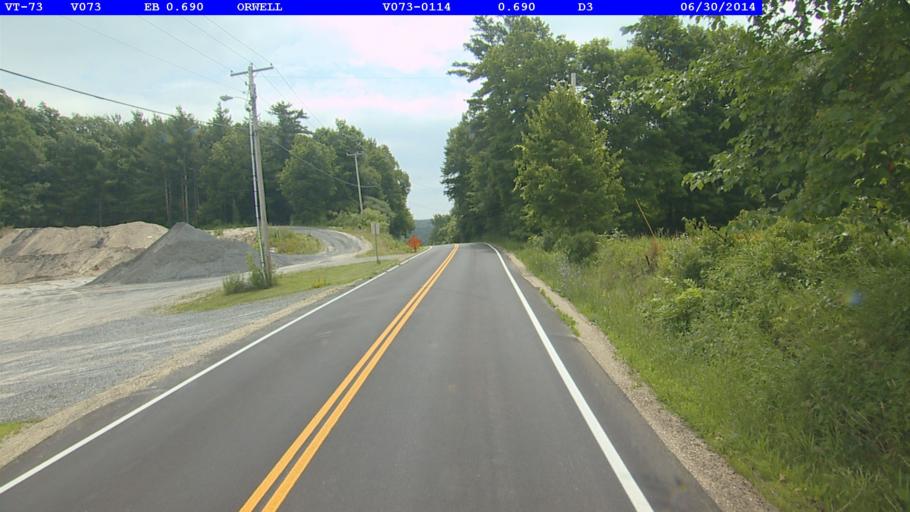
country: US
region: New York
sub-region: Essex County
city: Ticonderoga
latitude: 43.8034
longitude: -73.2918
